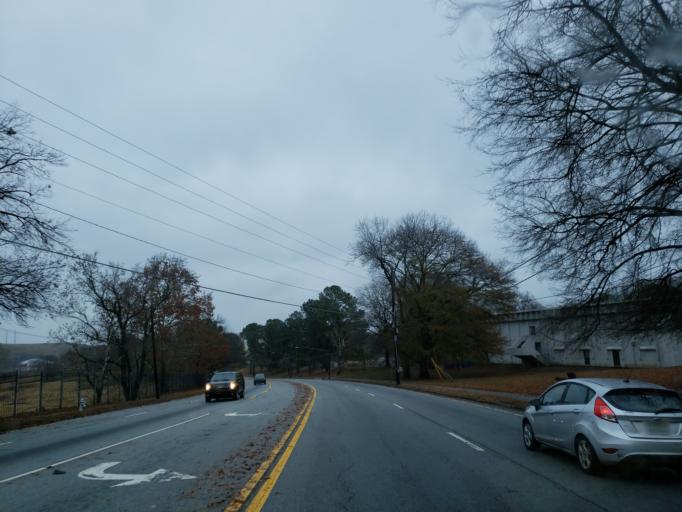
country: US
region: Georgia
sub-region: DeKalb County
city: Gresham Park
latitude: 33.7052
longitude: -84.3552
